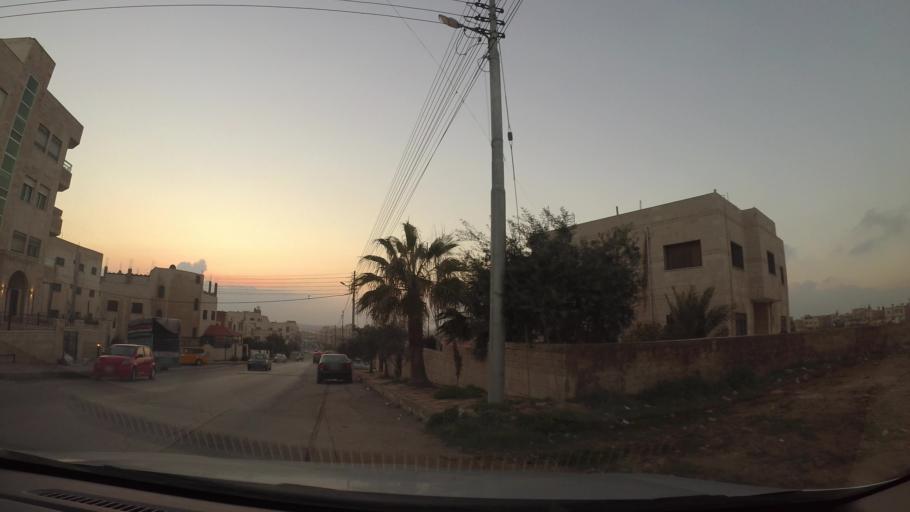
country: JO
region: Amman
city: Al Bunayyat ash Shamaliyah
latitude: 31.8944
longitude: 35.9236
